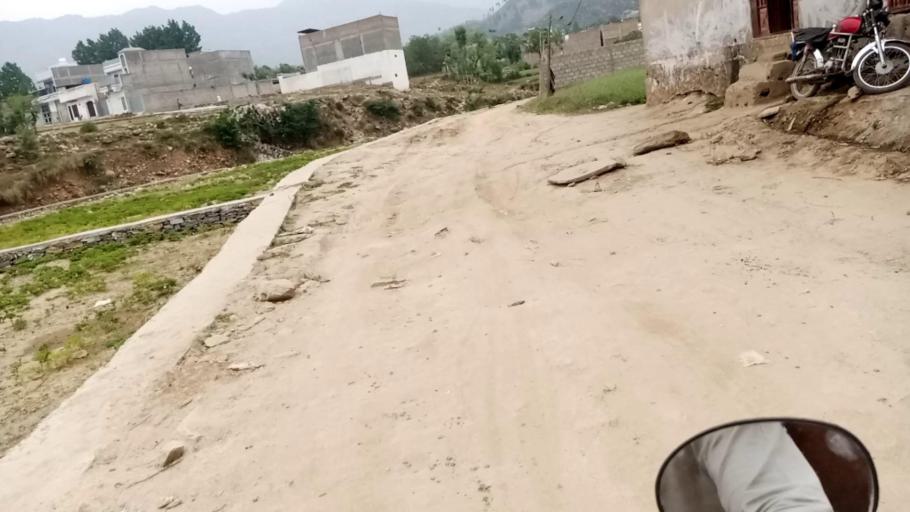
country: PK
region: Khyber Pakhtunkhwa
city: Saidu Sharif
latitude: 34.7543
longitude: 72.3863
